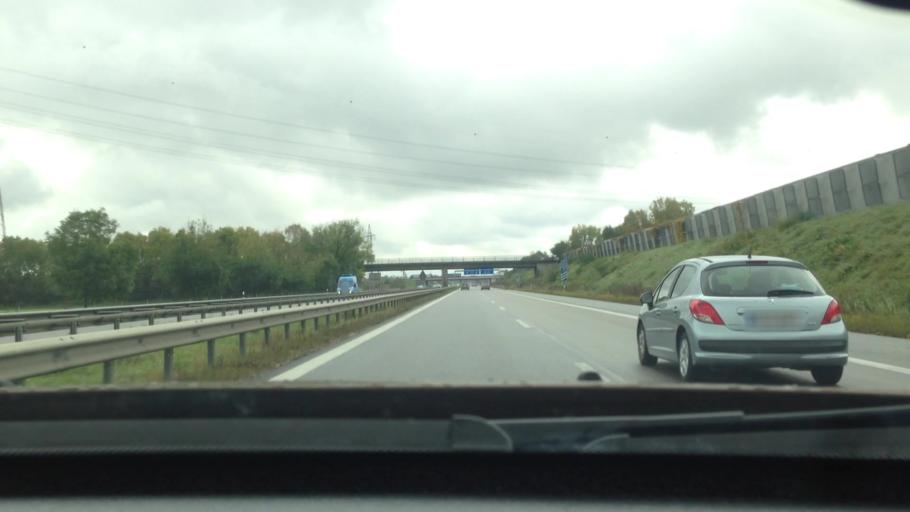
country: DE
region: Bavaria
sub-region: Upper Bavaria
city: Karlsfeld
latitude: 48.1862
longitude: 11.4248
